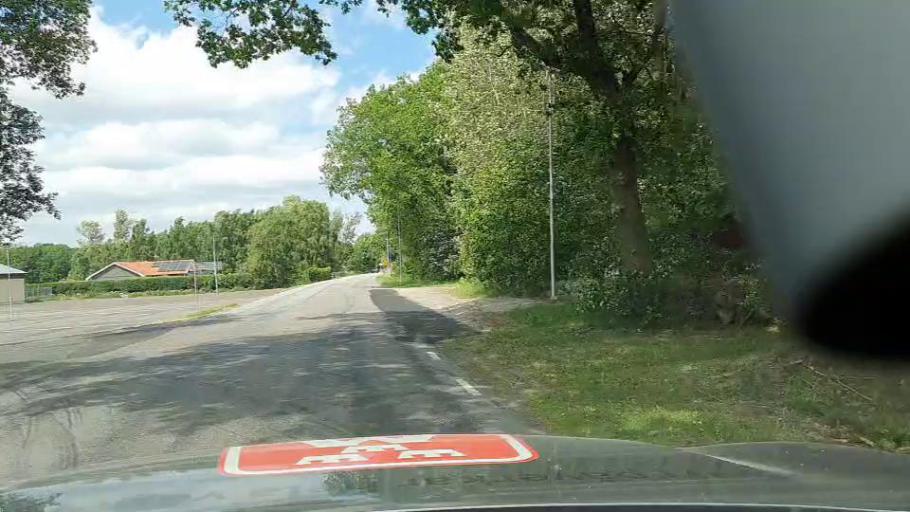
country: SE
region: Blekinge
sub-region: Karlshamns Kommun
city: Morrum
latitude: 56.1056
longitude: 14.6849
